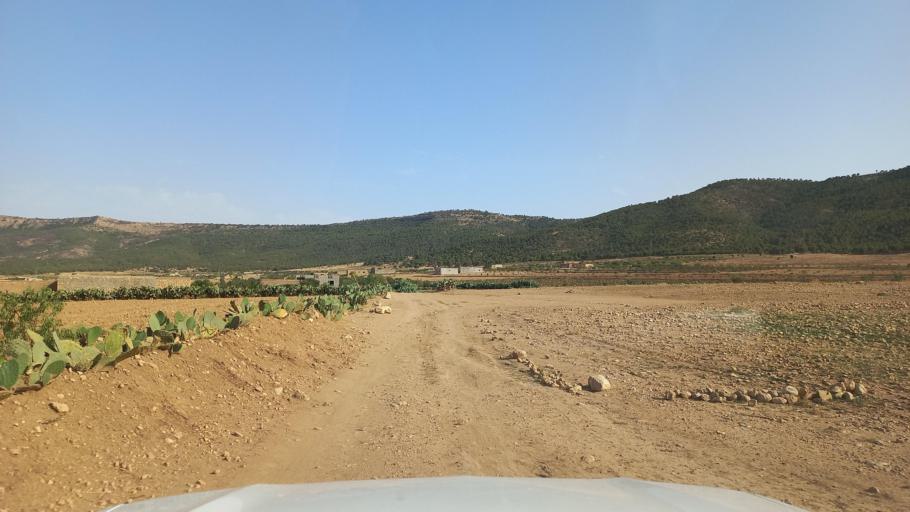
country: TN
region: Al Qasrayn
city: Kasserine
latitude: 35.3425
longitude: 8.8311
